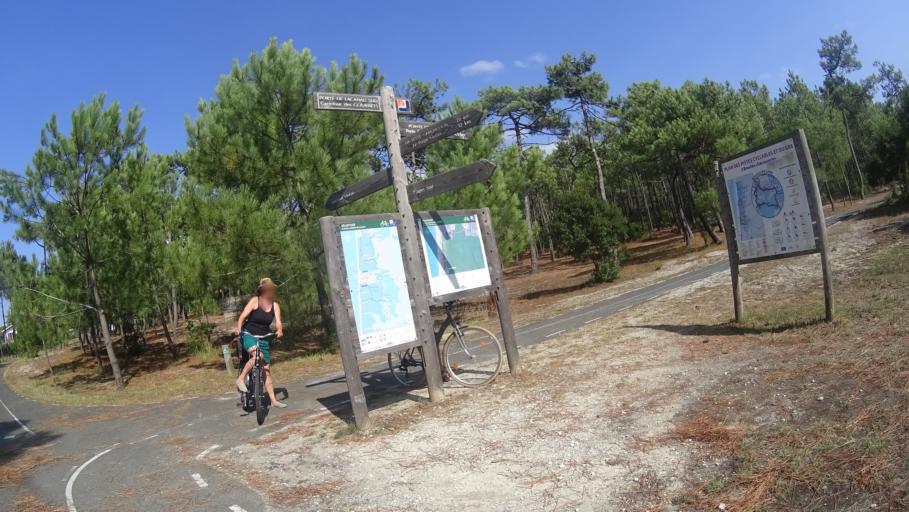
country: FR
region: Aquitaine
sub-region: Departement de la Gironde
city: Lacanau
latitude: 44.9912
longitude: -1.1979
